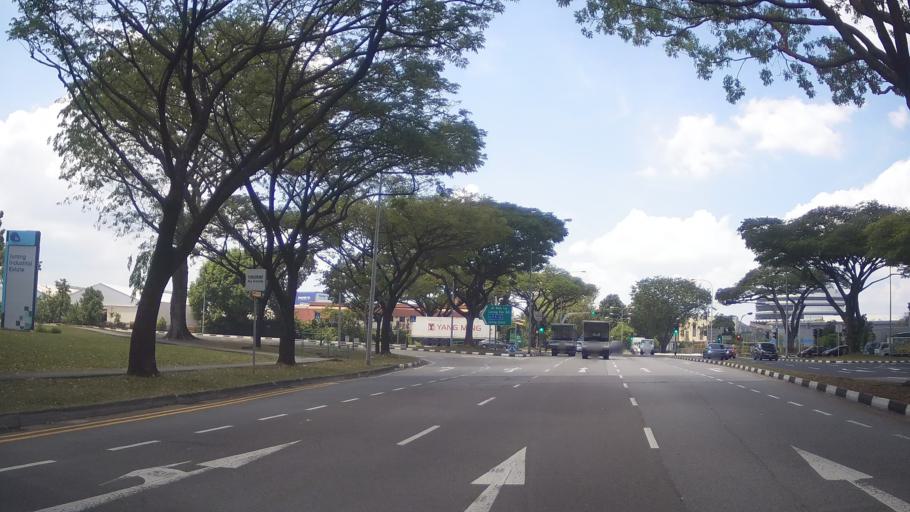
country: MY
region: Johor
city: Johor Bahru
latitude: 1.3284
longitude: 103.7095
